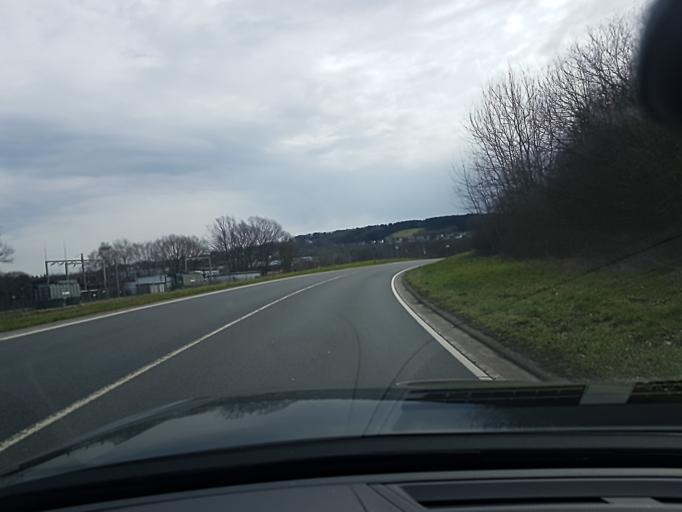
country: DE
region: North Rhine-Westphalia
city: Iserlohn
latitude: 51.4201
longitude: 7.6894
